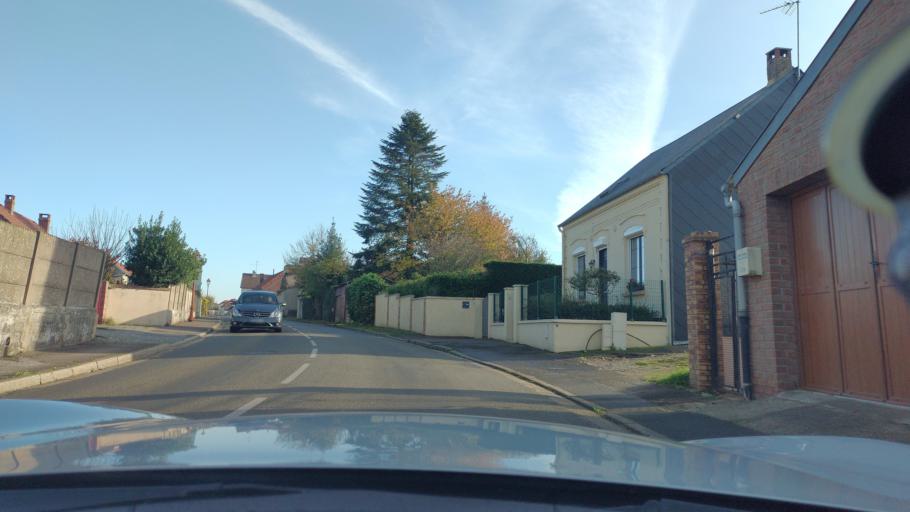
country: FR
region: Picardie
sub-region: Departement de la Somme
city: Fressenneville
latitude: 50.0688
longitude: 1.5686
